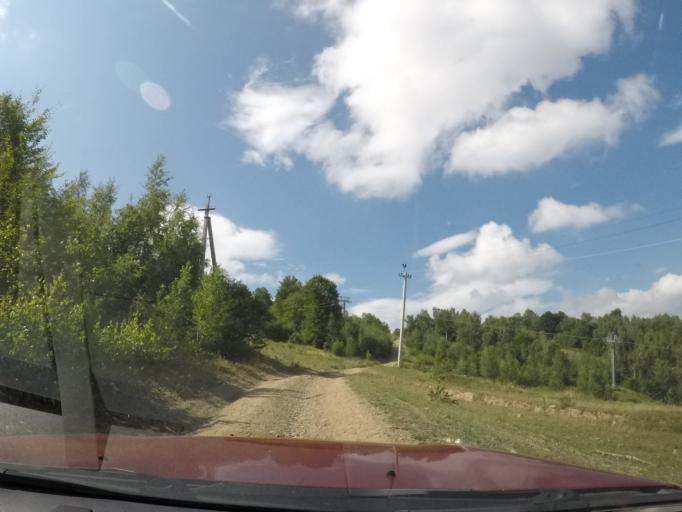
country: UA
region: Zakarpattia
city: Velykyi Bereznyi
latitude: 48.9403
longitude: 22.6678
